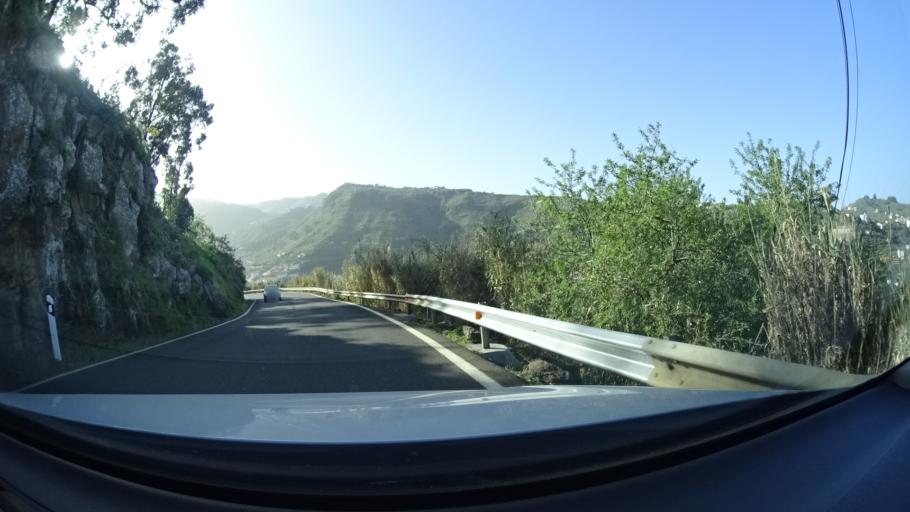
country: ES
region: Canary Islands
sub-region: Provincia de Las Palmas
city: Vega de San Mateo
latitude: 28.0190
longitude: -15.5424
